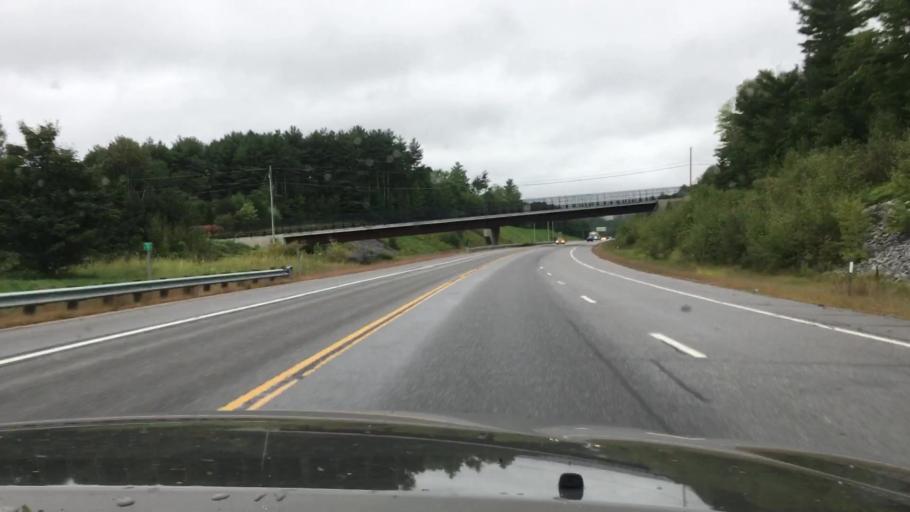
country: US
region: New Hampshire
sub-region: Hillsborough County
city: Hillsborough
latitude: 43.1163
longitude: -71.9189
